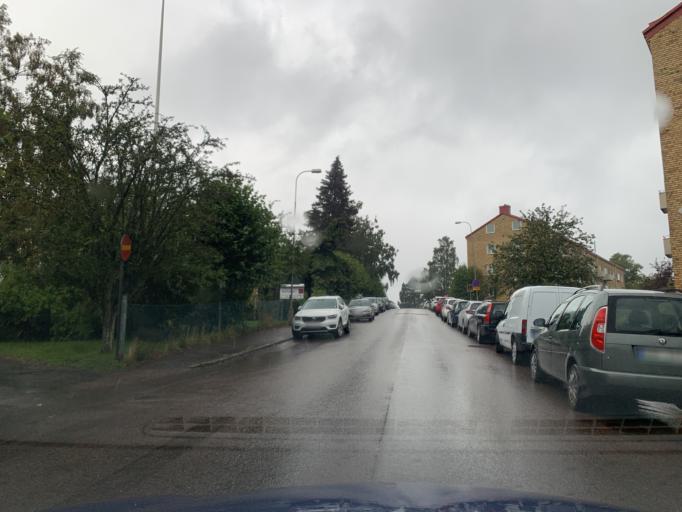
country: SE
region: Vaestra Goetaland
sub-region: Goteborg
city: Goeteborg
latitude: 57.7005
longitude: 12.0095
